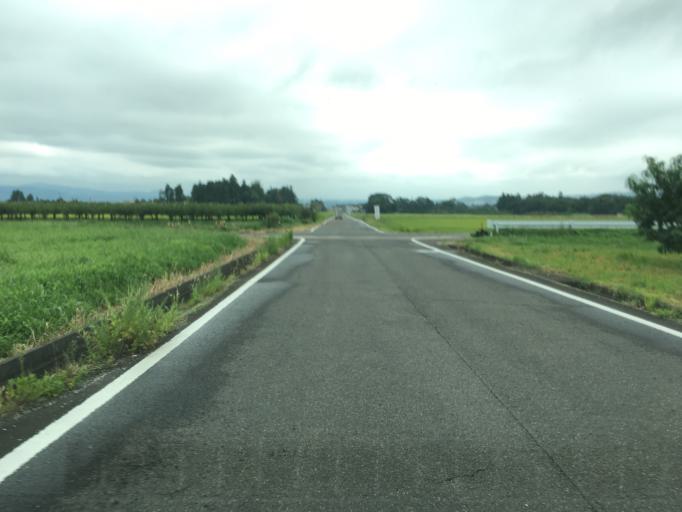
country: JP
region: Fukushima
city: Fukushima-shi
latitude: 37.7661
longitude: 140.3891
